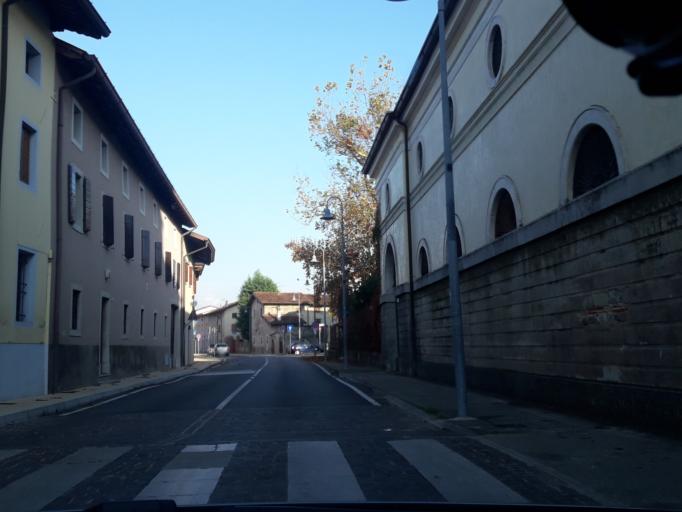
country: IT
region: Friuli Venezia Giulia
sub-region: Provincia di Udine
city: Pradamano
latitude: 46.0312
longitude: 13.3001
